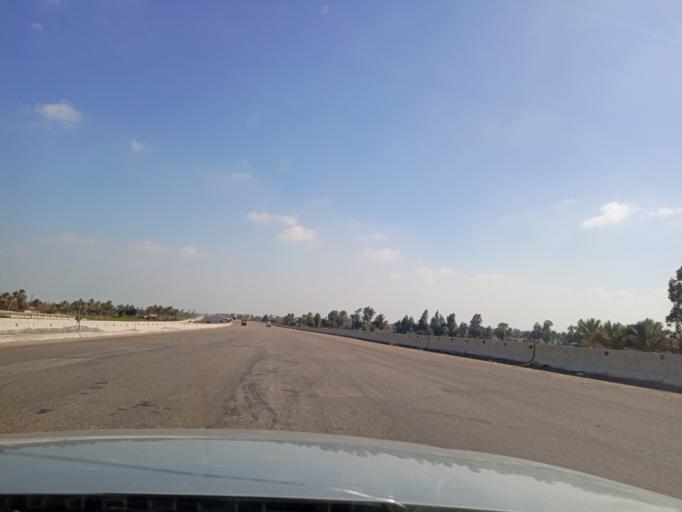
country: EG
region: Eastern Province
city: Mashtul as Suq
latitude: 30.4590
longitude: 31.3436
